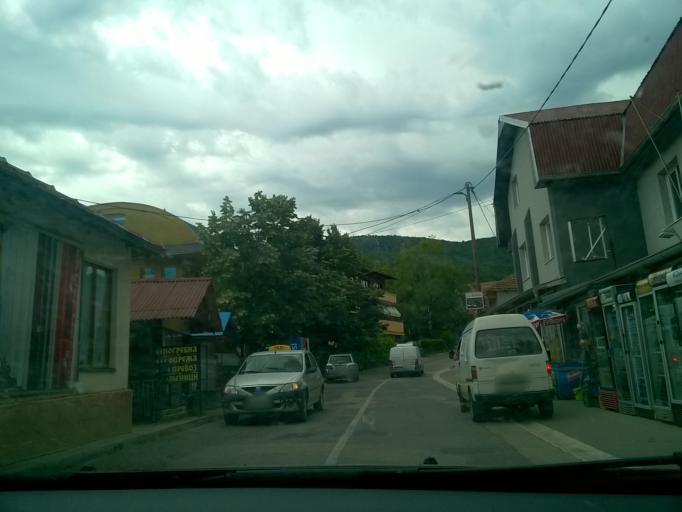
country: RS
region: Central Serbia
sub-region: Zajecarski Okrug
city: Soko Banja
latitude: 43.6461
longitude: 21.8754
